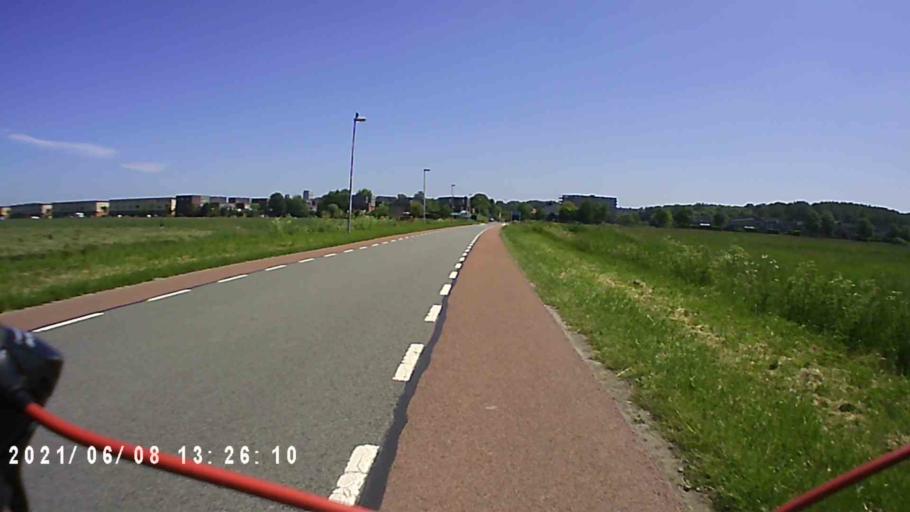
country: NL
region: Groningen
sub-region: Gemeente Zuidhorn
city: Aduard
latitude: 53.2269
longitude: 6.5076
